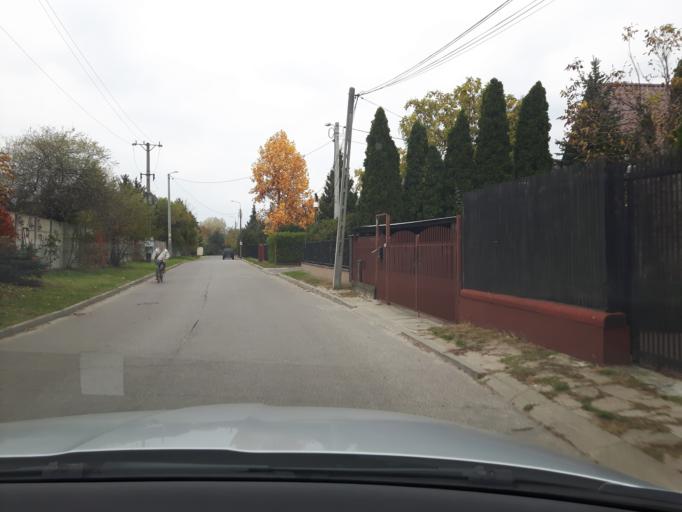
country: PL
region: Masovian Voivodeship
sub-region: Powiat wolominski
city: Zabki
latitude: 52.2888
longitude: 21.0946
